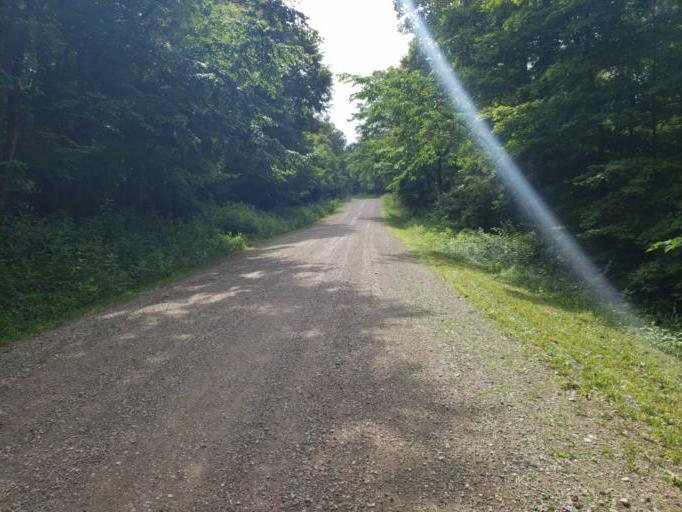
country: US
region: Ohio
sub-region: Washington County
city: Newport
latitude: 39.4601
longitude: -81.2202
